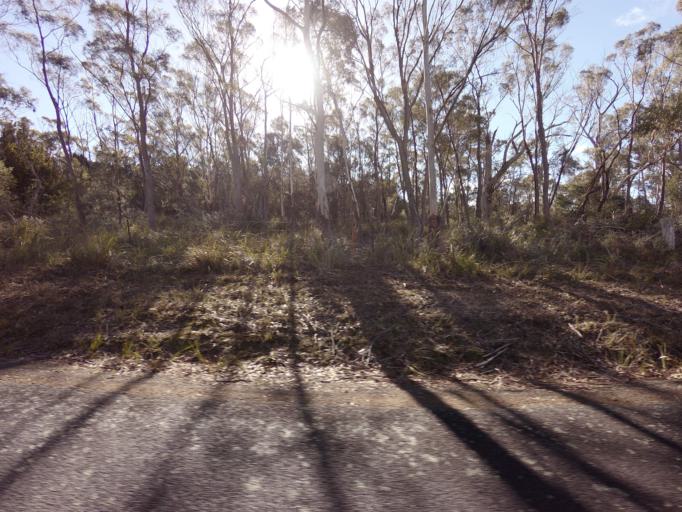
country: AU
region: Tasmania
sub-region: Sorell
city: Sorell
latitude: -42.3595
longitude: 147.9584
